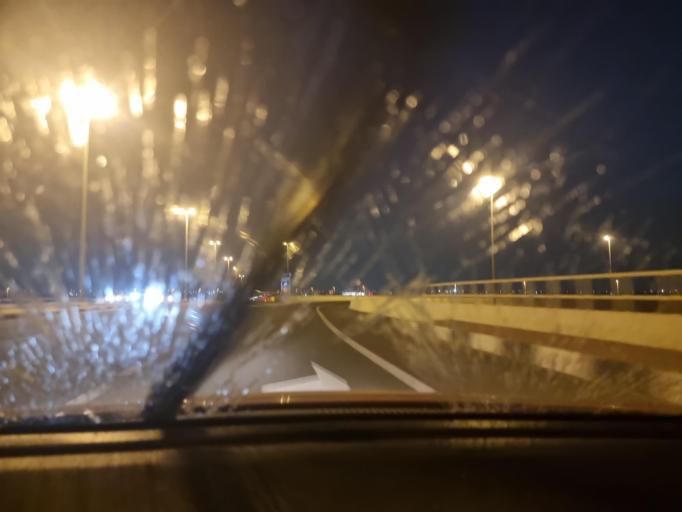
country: AE
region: Abu Dhabi
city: Abu Dhabi
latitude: 24.4137
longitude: 54.7146
